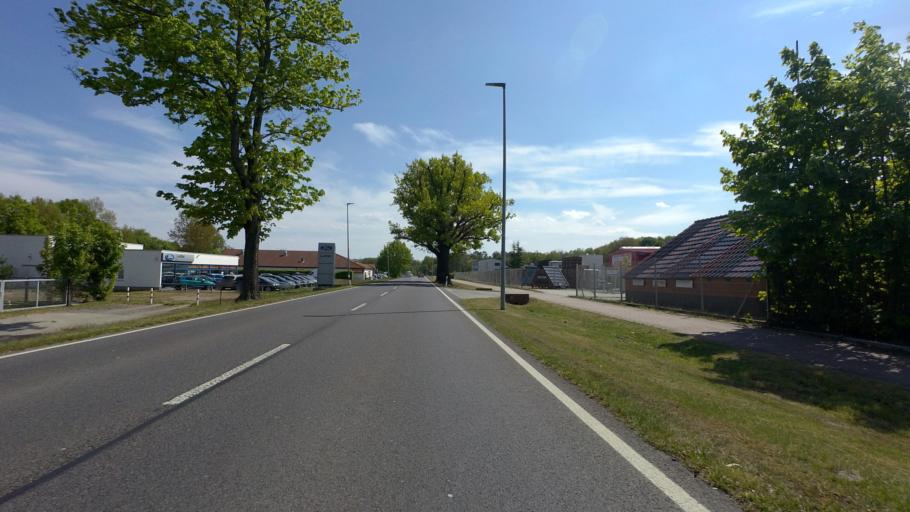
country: DE
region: Brandenburg
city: Tschernitz
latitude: 51.6043
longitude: 14.6100
